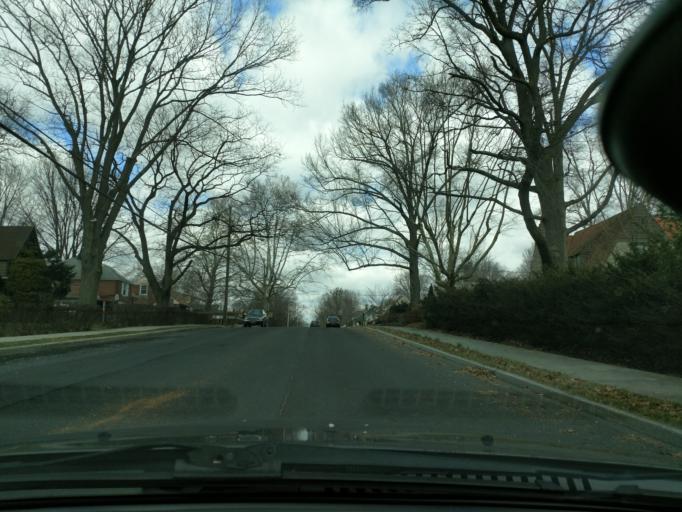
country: US
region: Pennsylvania
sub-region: Lebanon County
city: Lebanon South
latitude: 40.3344
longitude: -76.4058
